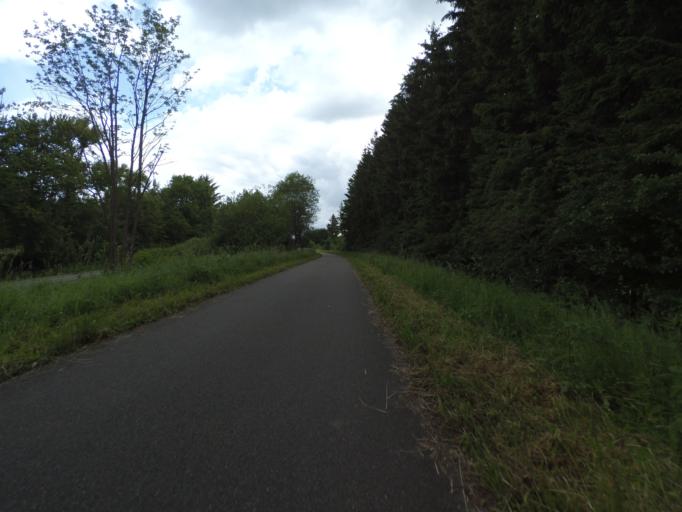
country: DE
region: North Rhine-Westphalia
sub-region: Regierungsbezirk Koln
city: Monschau
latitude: 50.5969
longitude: 6.2485
